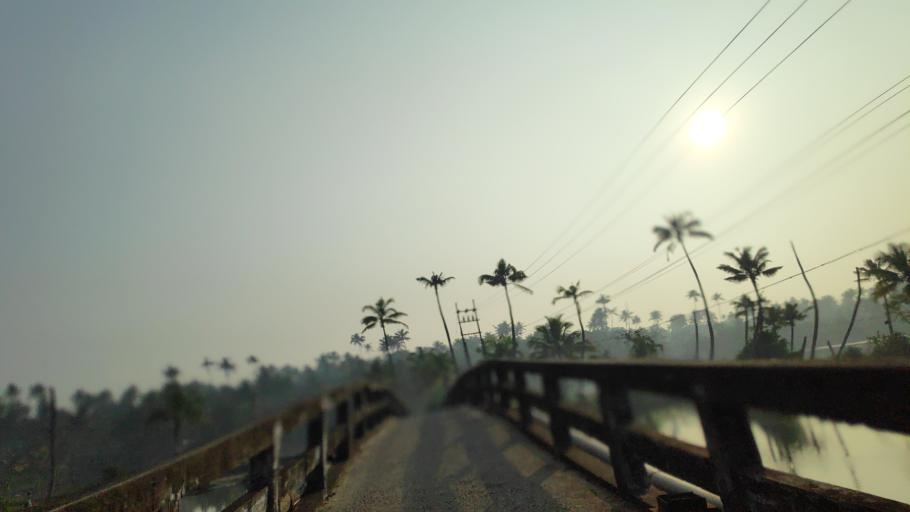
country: IN
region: Kerala
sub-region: Alappuzha
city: Vayalar
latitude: 9.7275
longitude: 76.2880
